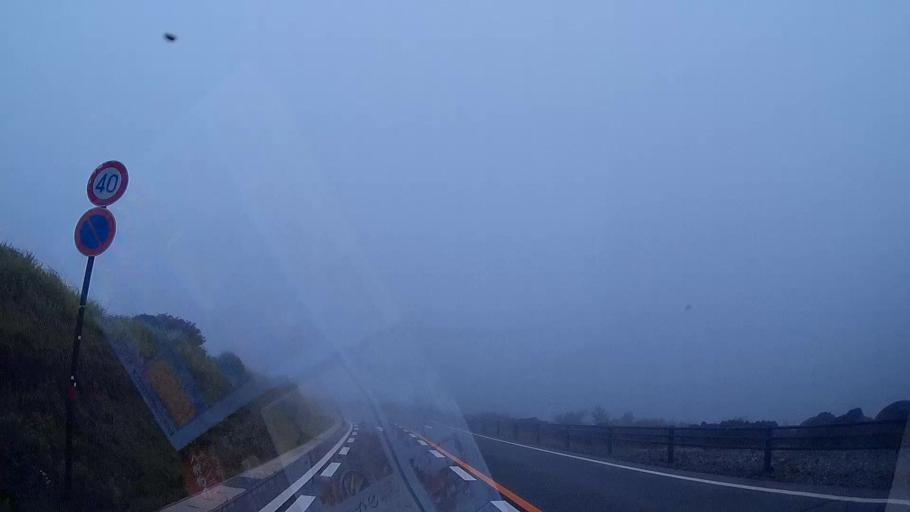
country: JP
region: Kumamoto
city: Aso
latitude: 32.8844
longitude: 131.0497
